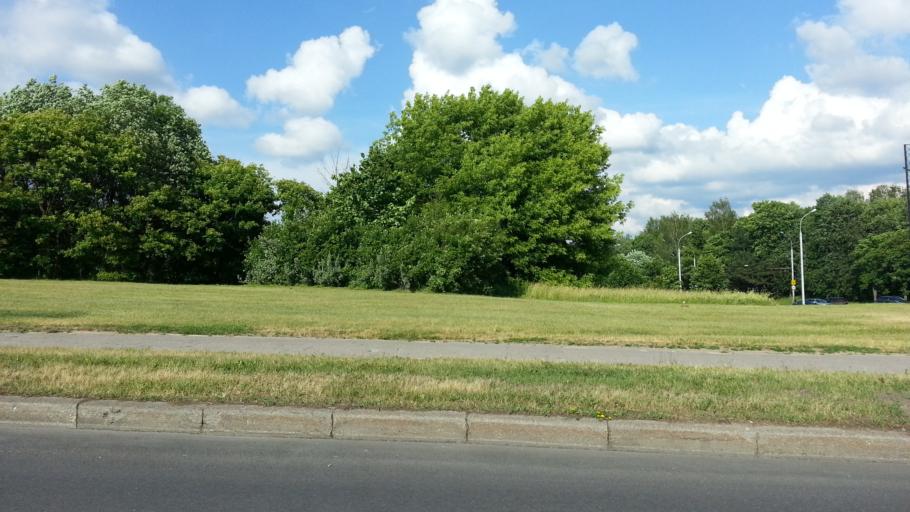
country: LT
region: Vilnius County
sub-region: Vilnius
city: Vilnius
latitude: 54.7210
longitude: 25.3020
